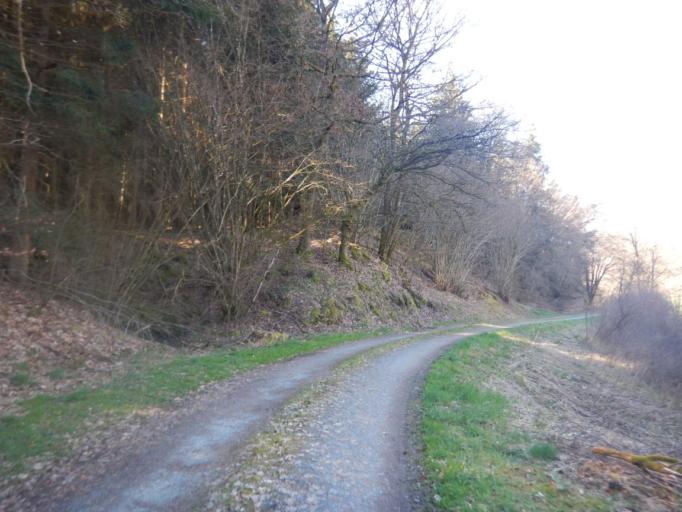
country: LU
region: Diekirch
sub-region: Canton de Wiltz
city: Eschweiler
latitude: 49.9847
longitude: 5.9681
